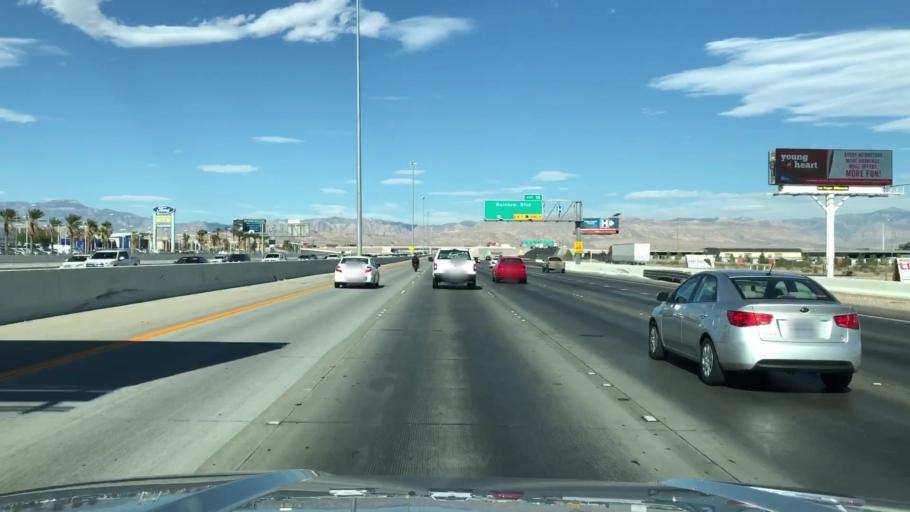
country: US
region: Nevada
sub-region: Clark County
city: Enterprise
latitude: 36.0667
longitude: -115.2336
